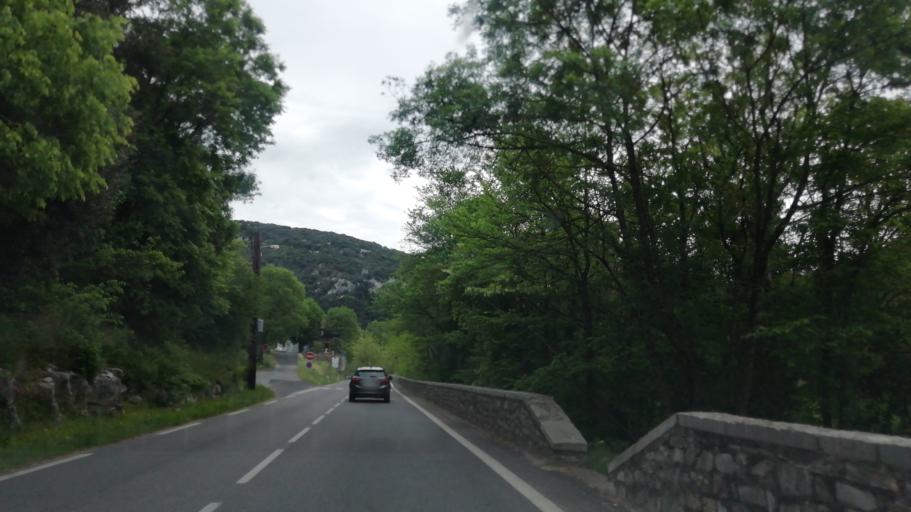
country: FR
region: Languedoc-Roussillon
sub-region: Departement de l'Herault
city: Laroque
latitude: 43.9203
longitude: 3.7256
